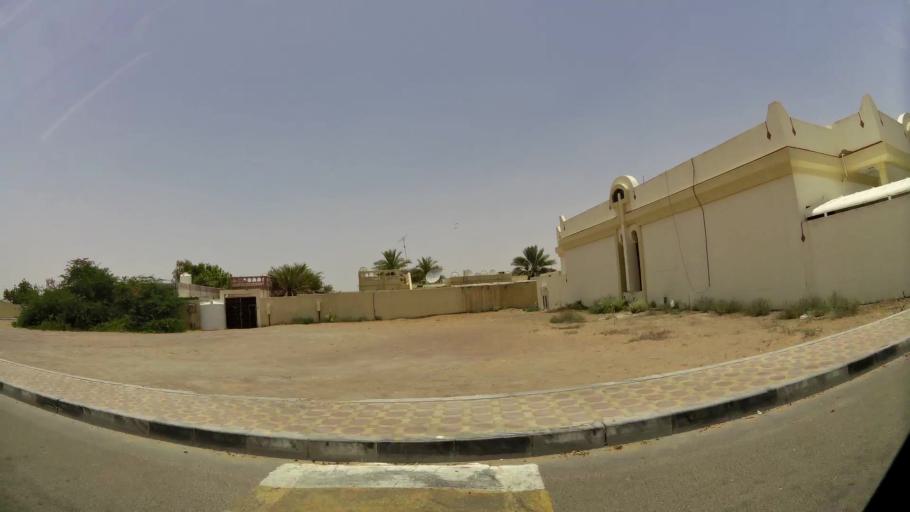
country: AE
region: Abu Dhabi
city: Al Ain
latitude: 24.2192
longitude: 55.7347
